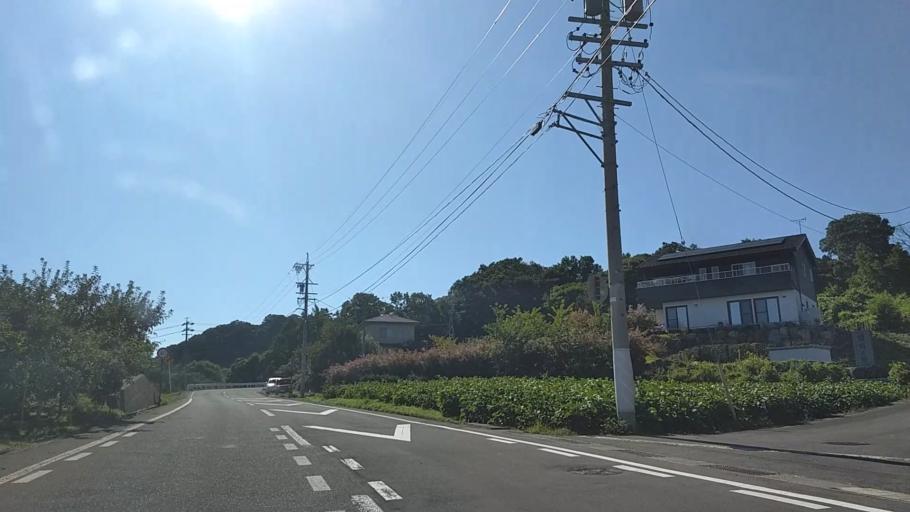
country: JP
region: Nagano
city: Nagano-shi
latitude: 36.5828
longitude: 138.1124
